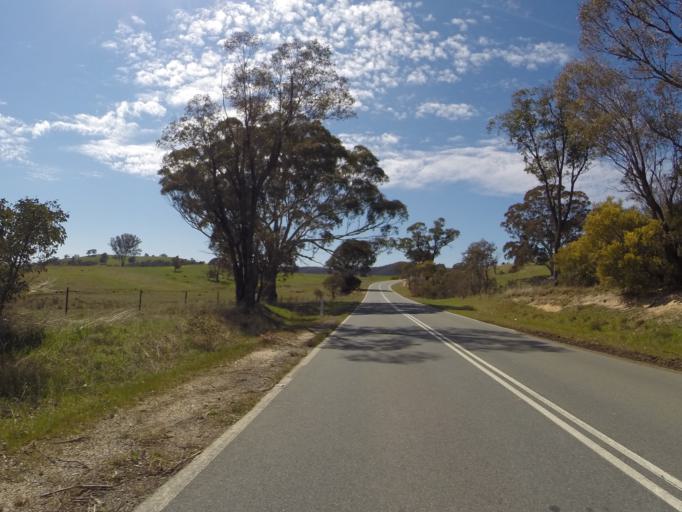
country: AU
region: Australian Capital Territory
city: Macarthur
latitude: -35.4132
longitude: 148.9710
